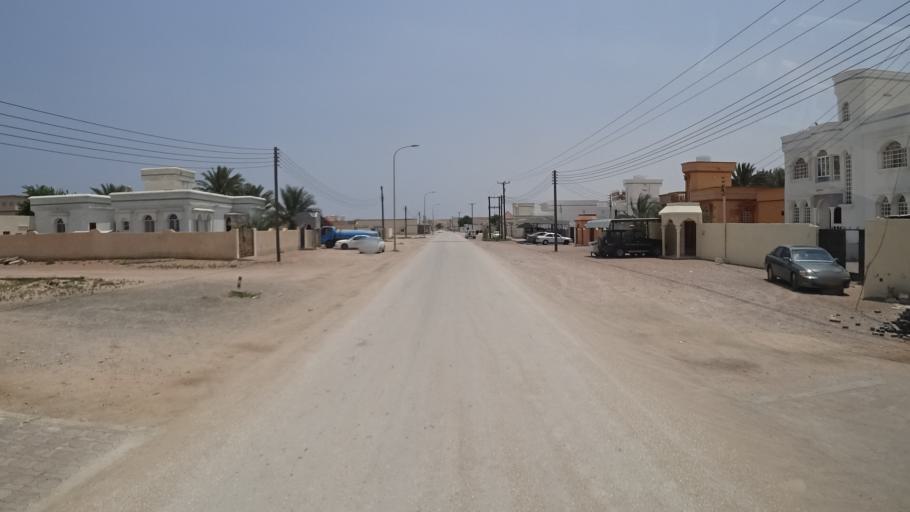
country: OM
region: Ash Sharqiyah
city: Sur
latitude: 22.5129
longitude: 59.7980
